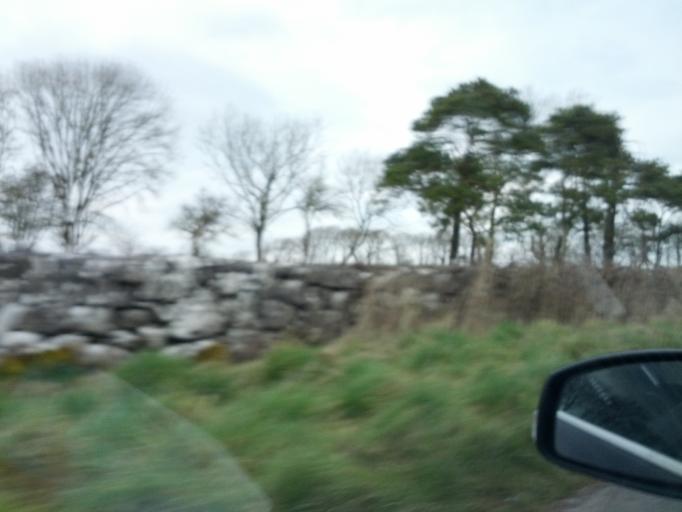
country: IE
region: Connaught
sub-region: County Galway
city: Oranmore
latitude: 53.2610
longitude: -8.8297
